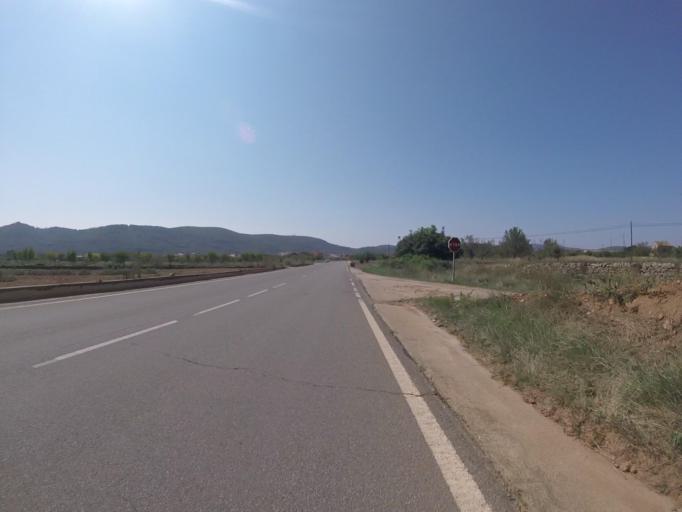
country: ES
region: Valencia
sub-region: Provincia de Castello
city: Adzaneta
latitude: 40.2254
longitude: -0.1732
